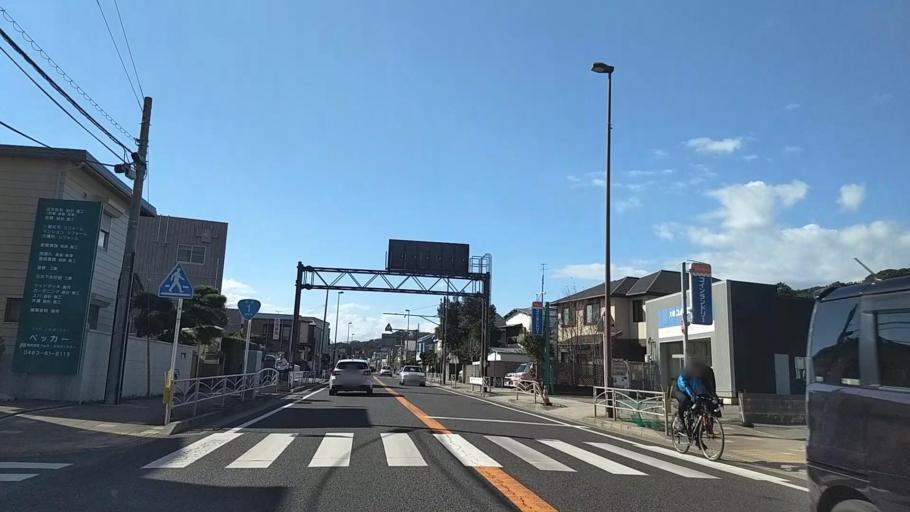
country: JP
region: Kanagawa
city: Oiso
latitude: 35.3142
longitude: 139.3206
